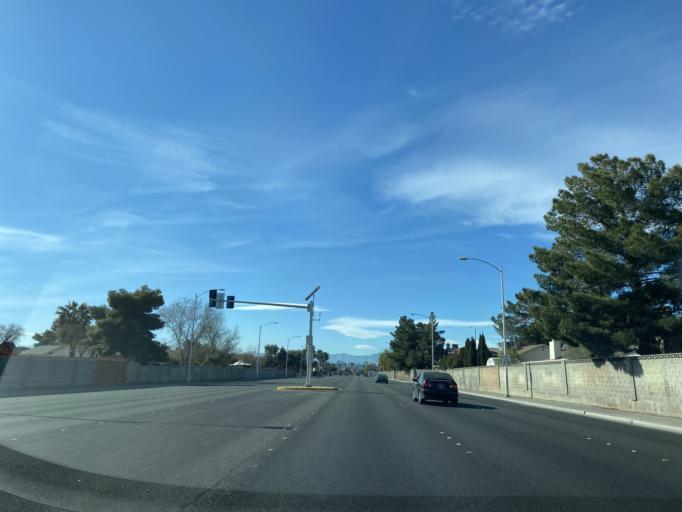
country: US
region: Nevada
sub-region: Clark County
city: Sunrise Manor
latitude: 36.1738
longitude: -115.0723
